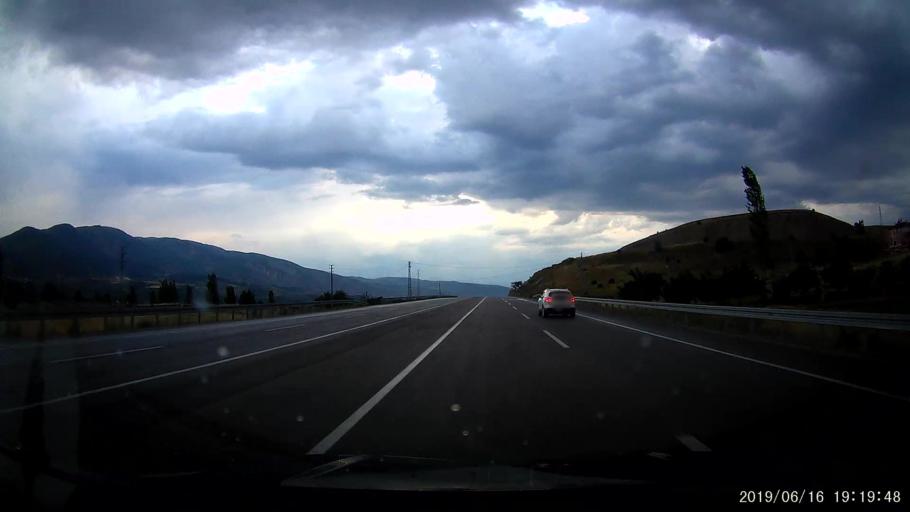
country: TR
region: Sivas
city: Akincilar
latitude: 40.0949
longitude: 38.4183
